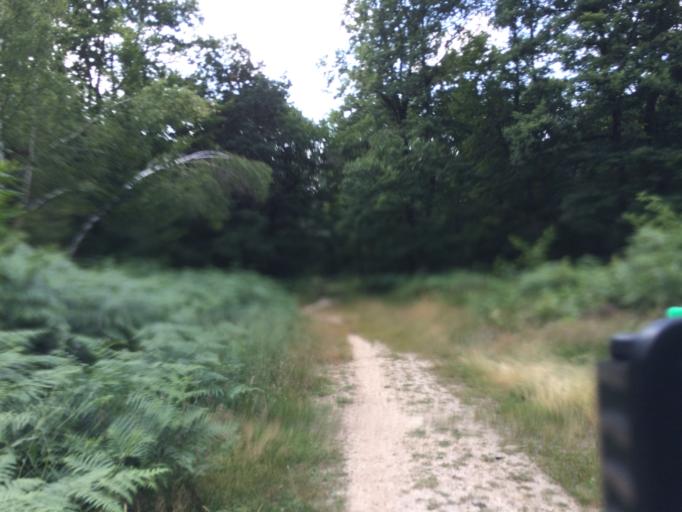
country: FR
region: Ile-de-France
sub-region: Departement de l'Essonne
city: Soisy-sur-Seine
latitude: 48.6655
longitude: 2.4487
